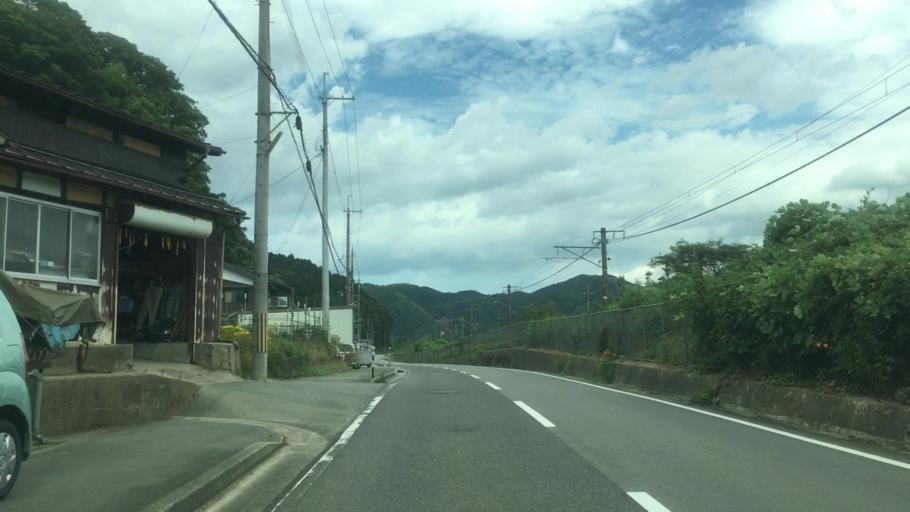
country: JP
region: Hyogo
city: Toyooka
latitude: 35.5671
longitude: 134.8037
